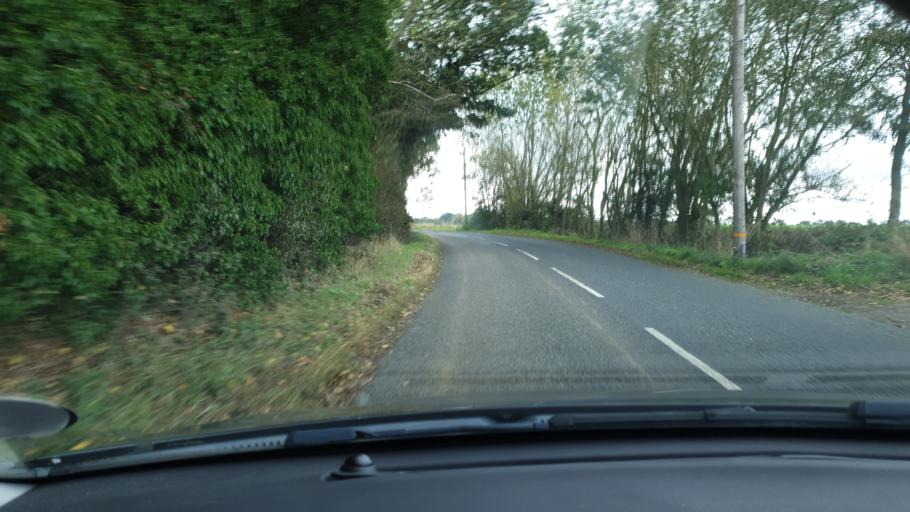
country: GB
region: England
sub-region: Essex
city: Manningtree
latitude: 51.9290
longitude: 1.0488
